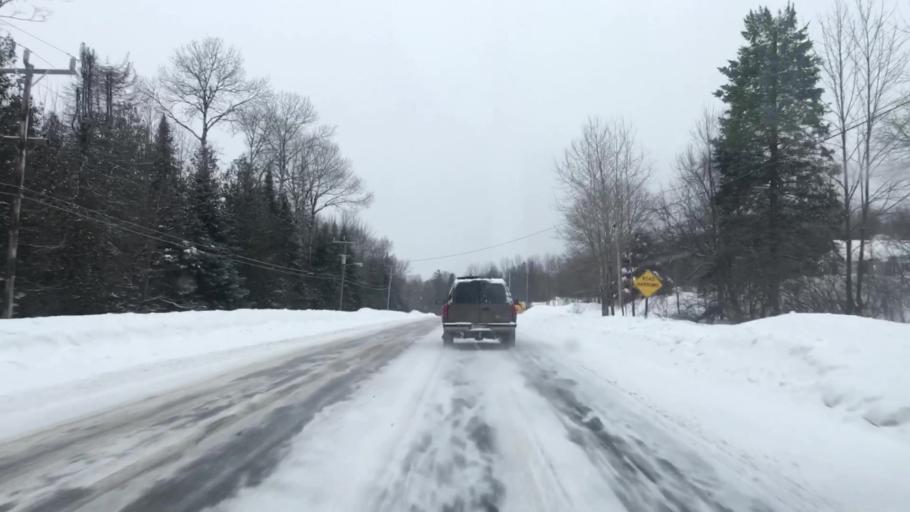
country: US
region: Maine
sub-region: Penobscot County
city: Medway
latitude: 45.5882
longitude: -68.4390
